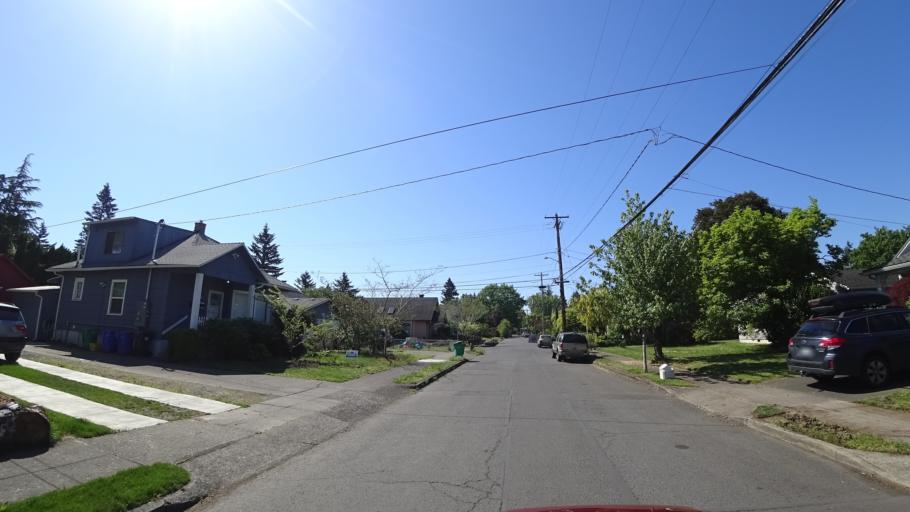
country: US
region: Oregon
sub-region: Multnomah County
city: Lents
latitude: 45.4871
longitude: -122.6014
